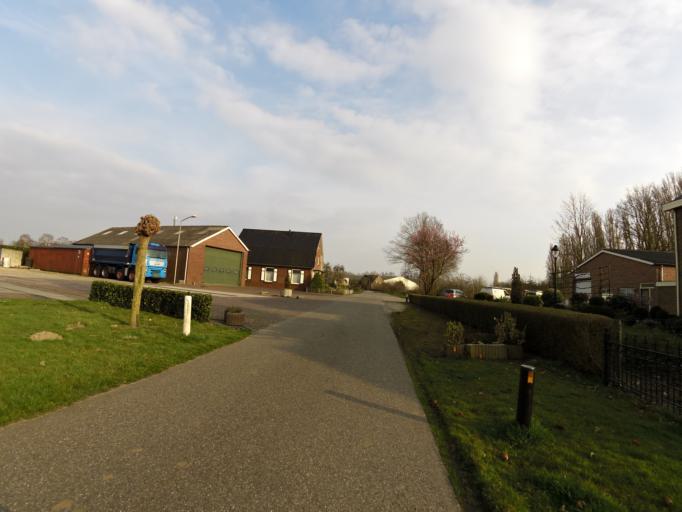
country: NL
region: Gelderland
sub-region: Gemeente Zevenaar
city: Zevenaar
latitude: 51.9451
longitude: 6.1176
